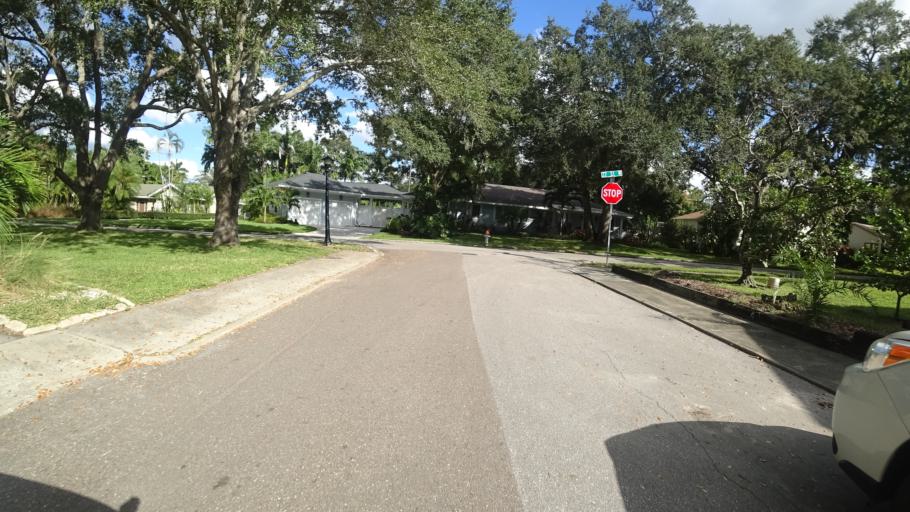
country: US
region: Florida
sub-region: Manatee County
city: Bradenton
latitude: 27.4972
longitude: -82.5839
